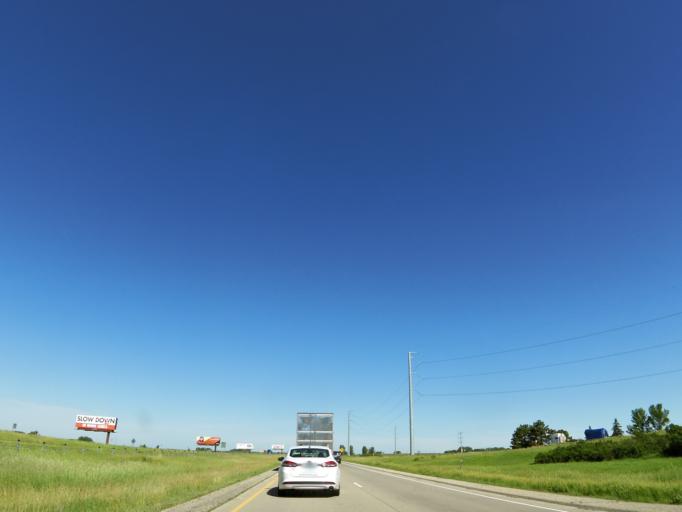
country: US
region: Minnesota
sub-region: Otter Tail County
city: Pelican Rapids
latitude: 46.4833
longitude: -96.2811
